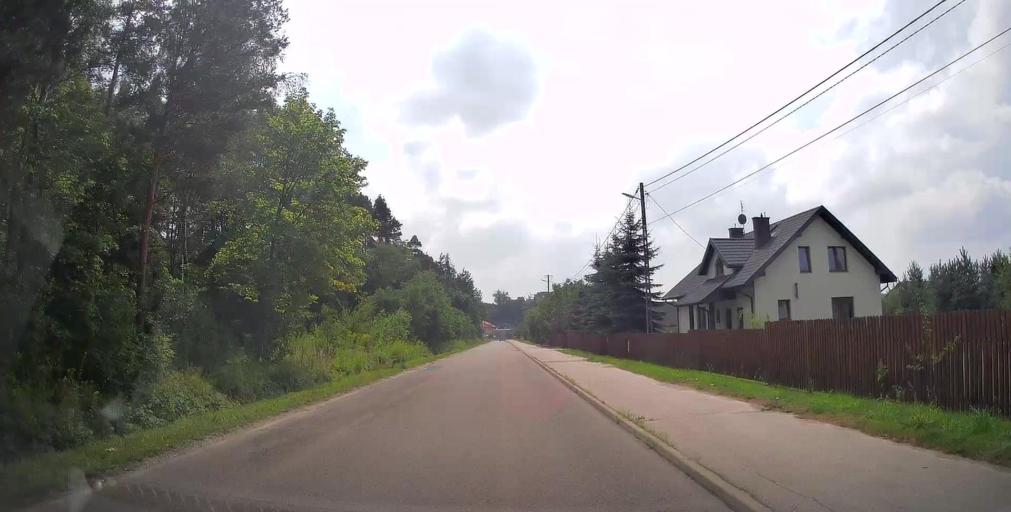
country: PL
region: Masovian Voivodeship
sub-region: Powiat bialobrzeski
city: Sucha
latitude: 51.6252
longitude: 20.9531
